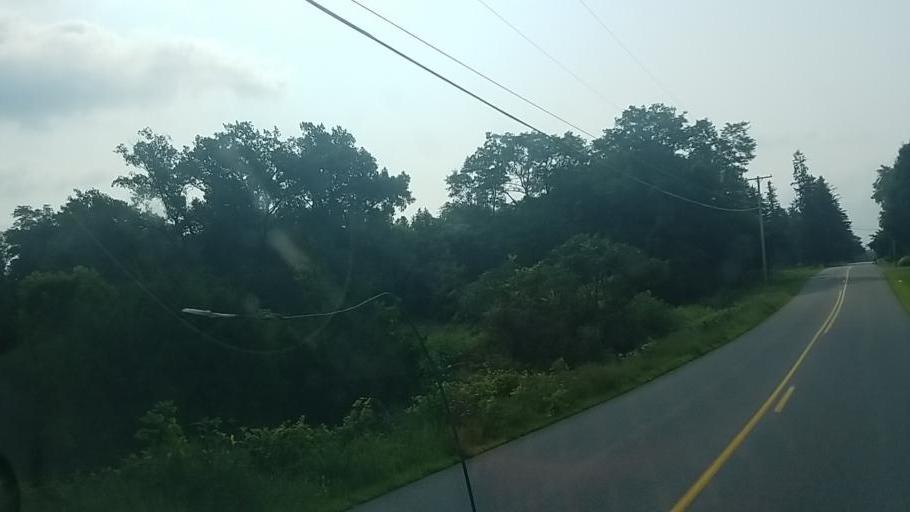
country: US
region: New York
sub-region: Montgomery County
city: Fonda
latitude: 42.9581
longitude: -74.4160
